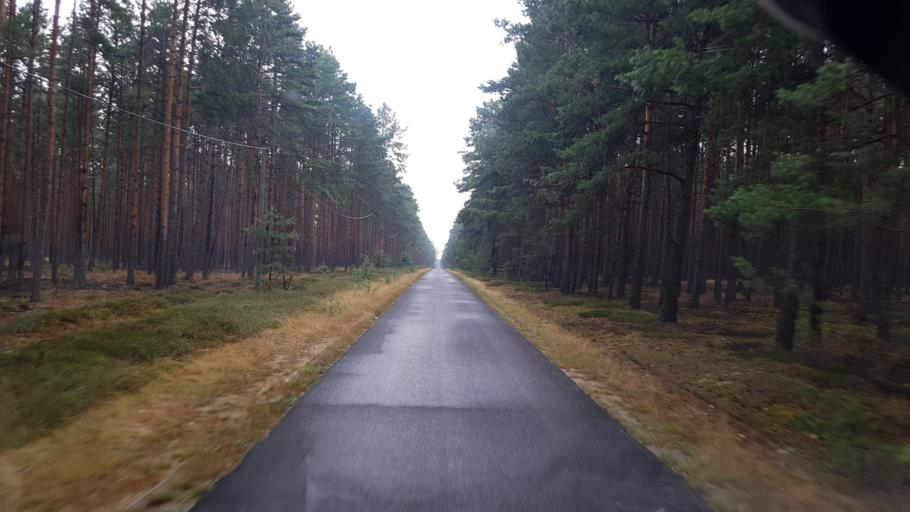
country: DE
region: Brandenburg
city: Finsterwalde
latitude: 51.6481
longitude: 13.7843
